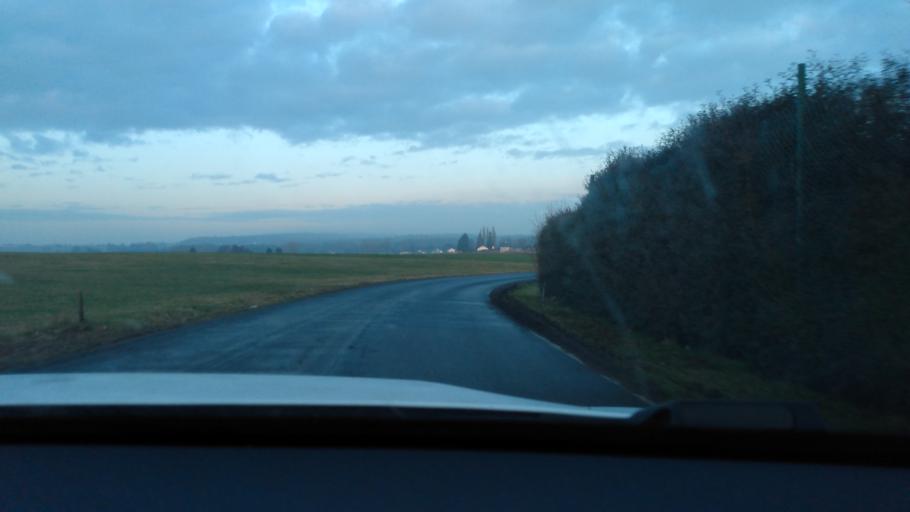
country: DE
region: Rheinland-Pfalz
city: Kircheib
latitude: 50.6864
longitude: 7.4504
